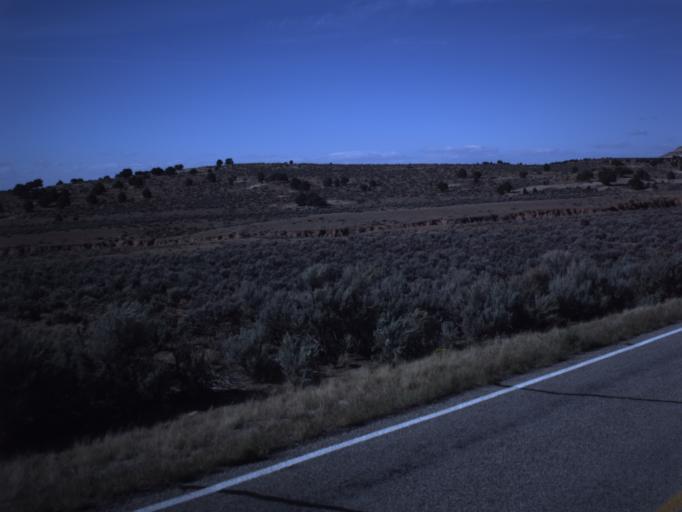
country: US
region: Utah
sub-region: San Juan County
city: Monticello
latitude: 38.0259
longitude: -109.4245
